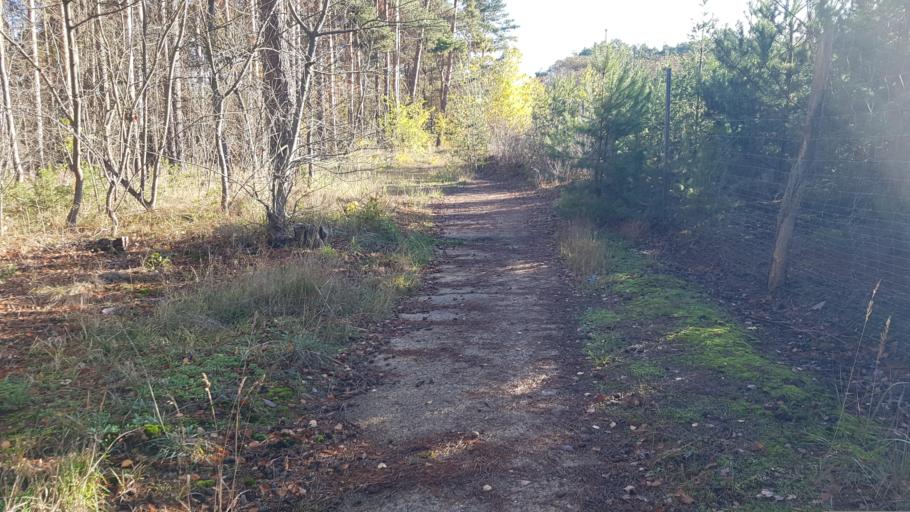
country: DE
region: Brandenburg
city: Schlieben
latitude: 51.7400
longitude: 13.3854
